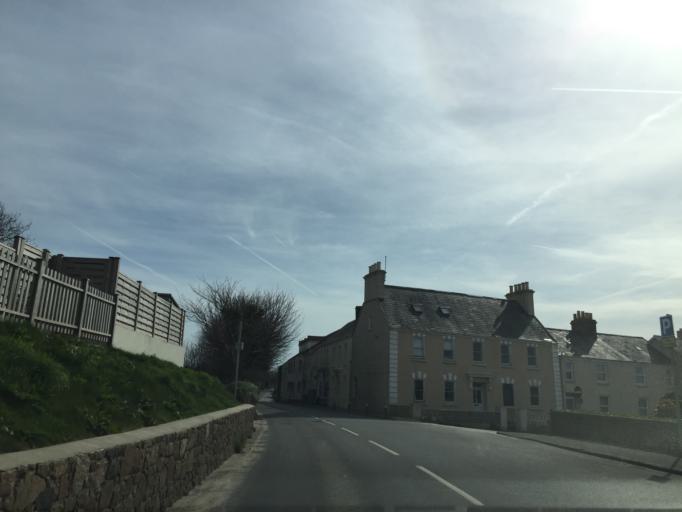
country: JE
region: St Helier
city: Saint Helier
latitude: 49.2330
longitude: -2.0895
